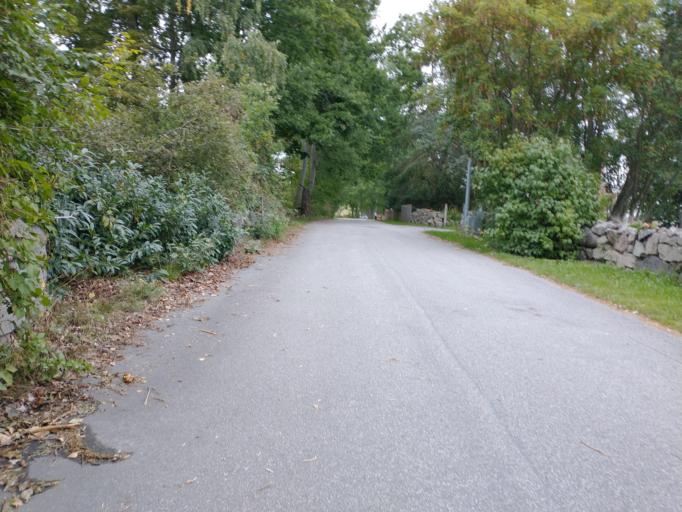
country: SE
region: Kalmar
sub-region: Kalmar Kommun
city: Lindsdal
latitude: 56.7862
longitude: 16.3002
